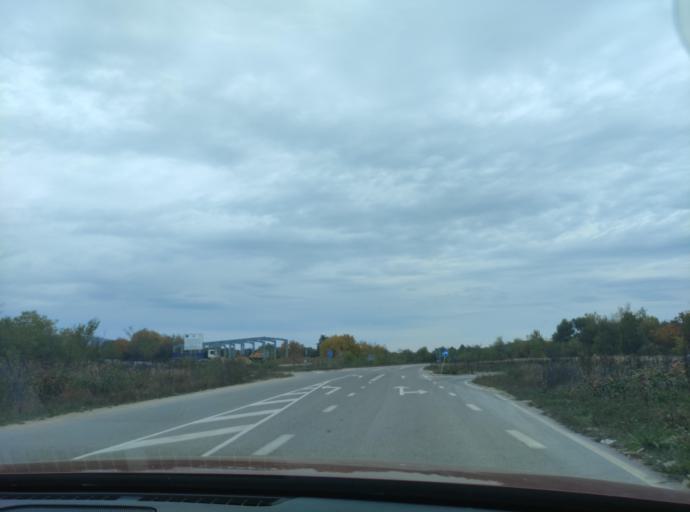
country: BG
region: Montana
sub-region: Obshtina Berkovitsa
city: Berkovitsa
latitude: 43.2431
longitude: 23.1639
